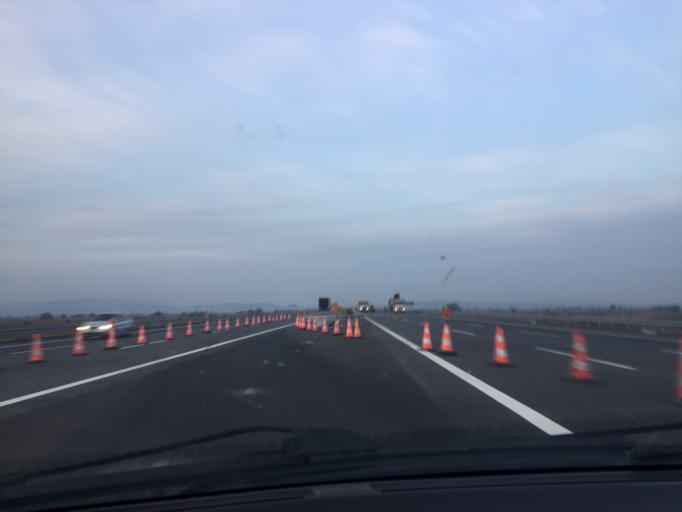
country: TR
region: Manisa
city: Halitpasa
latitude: 38.7224
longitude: 27.6523
